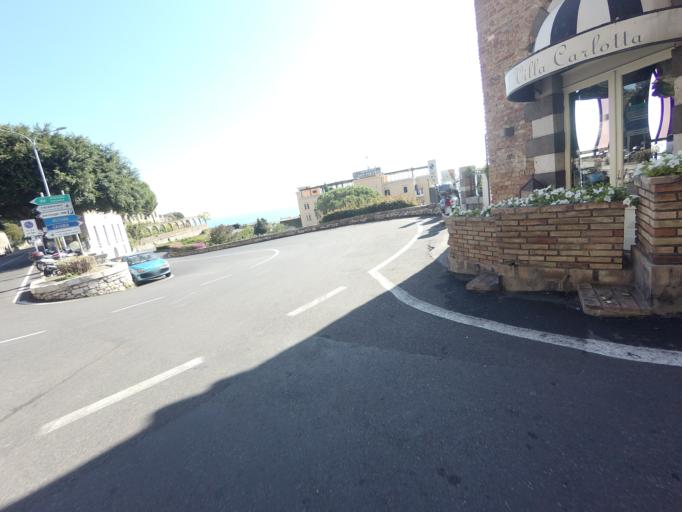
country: IT
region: Sicily
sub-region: Messina
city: Taormina
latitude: 37.8505
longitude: 15.2941
